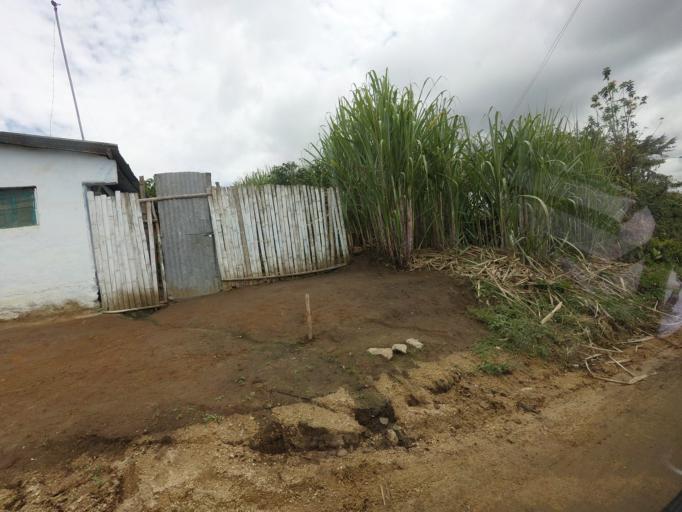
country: CO
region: Huila
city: Isnos
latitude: 1.9556
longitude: -76.2910
